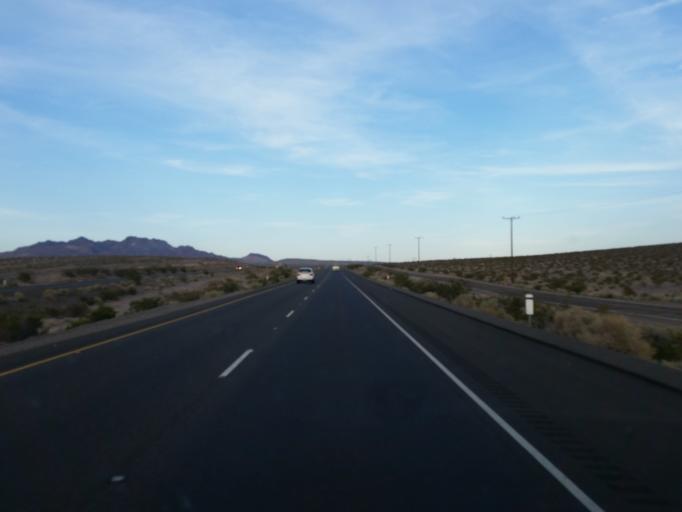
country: US
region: California
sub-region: San Bernardino County
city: Fort Irwin
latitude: 34.7826
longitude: -116.4127
